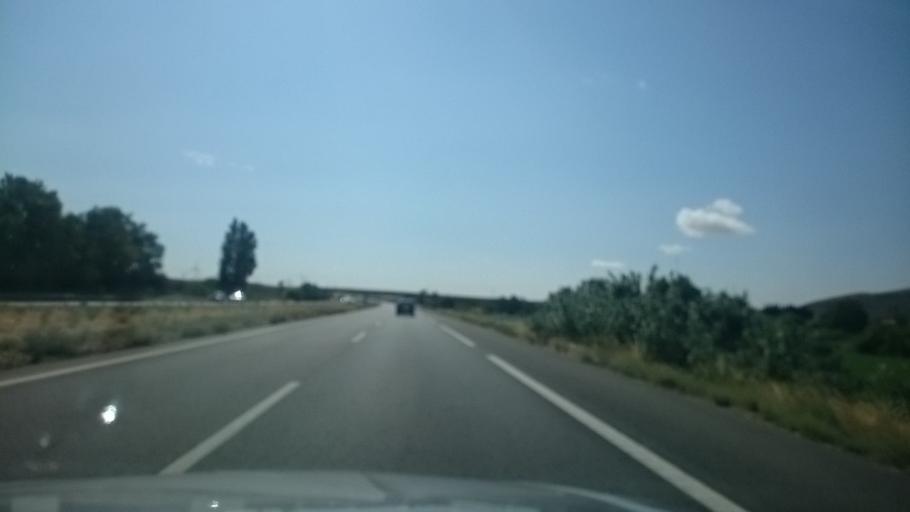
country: ES
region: Aragon
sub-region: Provincia de Zaragoza
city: Mallen
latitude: 41.8942
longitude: -1.4330
